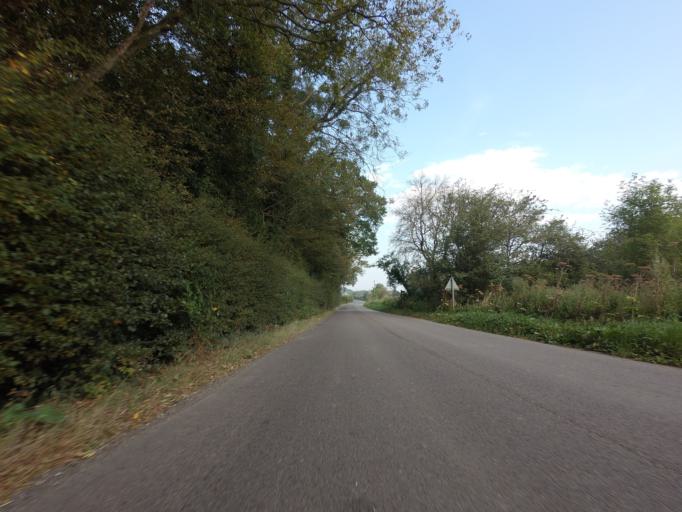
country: GB
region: England
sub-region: Kent
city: Ashford
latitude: 51.1075
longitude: 0.7919
